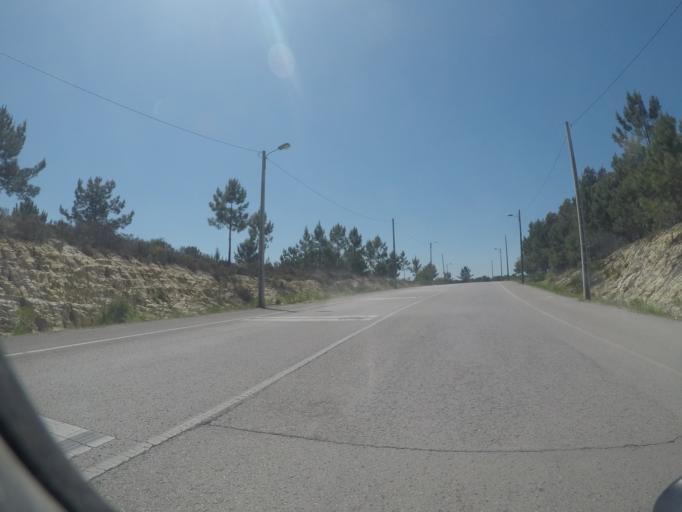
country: PT
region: Setubal
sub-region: Almada
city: Charneca
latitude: 38.5941
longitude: -9.1593
